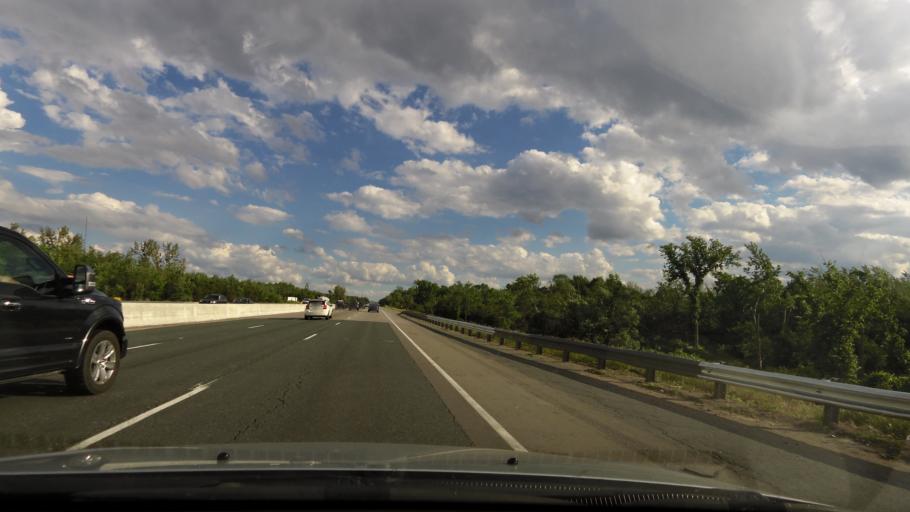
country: CA
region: Ontario
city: Bradford West Gwillimbury
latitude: 44.1736
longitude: -79.6443
